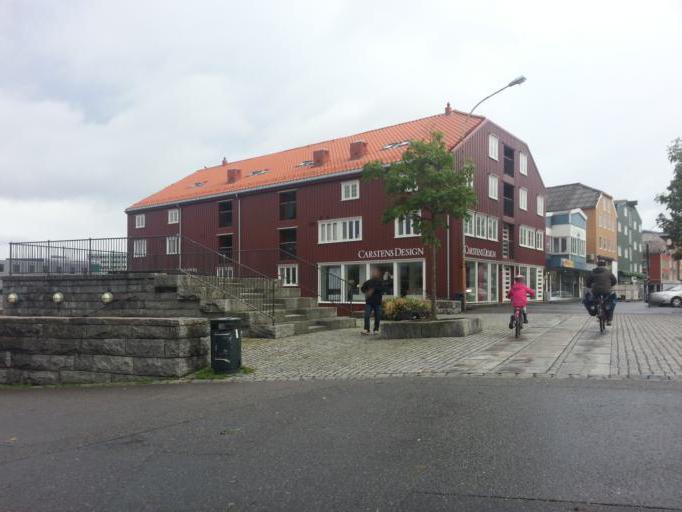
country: NO
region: Sor-Trondelag
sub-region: Trondheim
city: Trondheim
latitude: 63.4344
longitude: 10.3952
